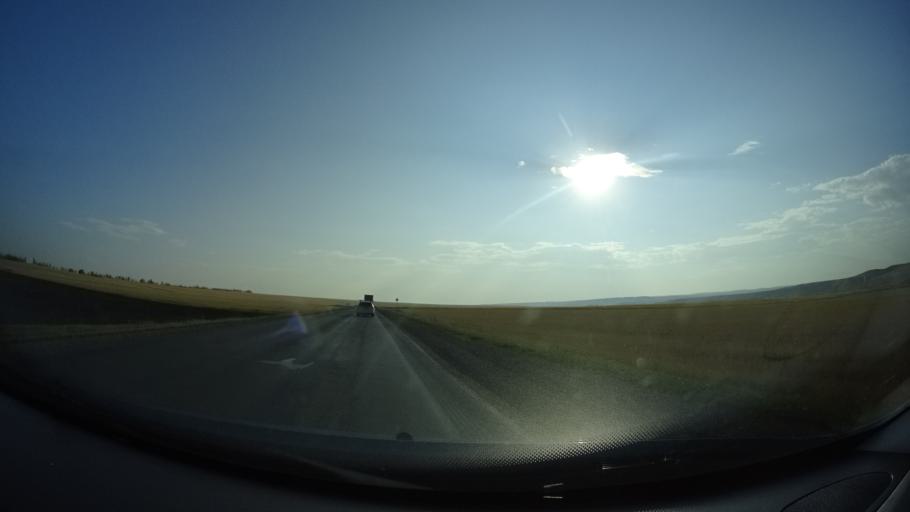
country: RU
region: Orenburg
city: Severnoye
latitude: 54.1248
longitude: 52.5617
